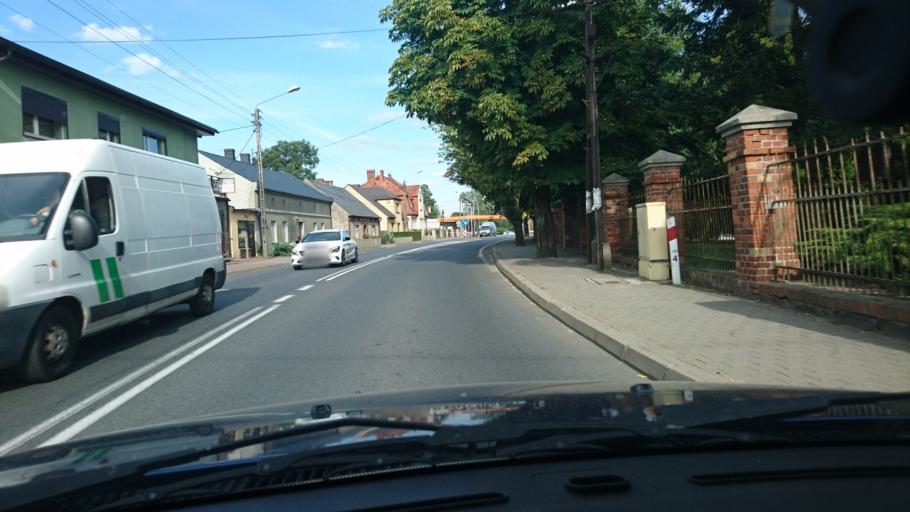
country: PL
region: Greater Poland Voivodeship
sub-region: Powiat krotoszynski
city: Kobylin
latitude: 51.7160
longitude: 17.2311
